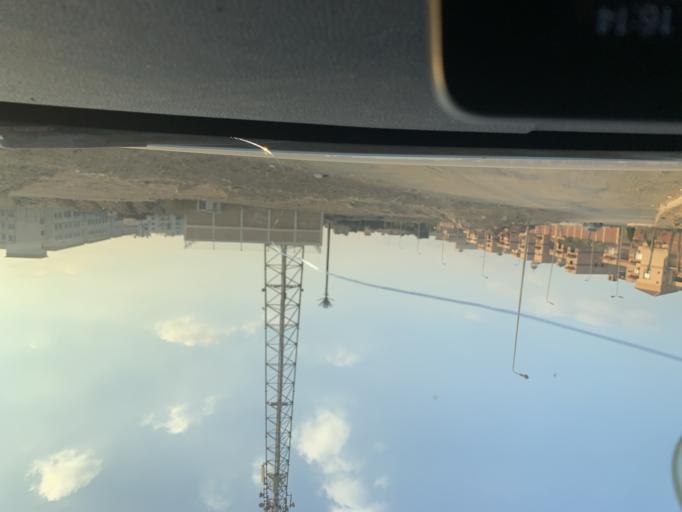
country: EG
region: Muhafazat al Qalyubiyah
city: Al Khankah
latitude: 30.0214
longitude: 31.4813
